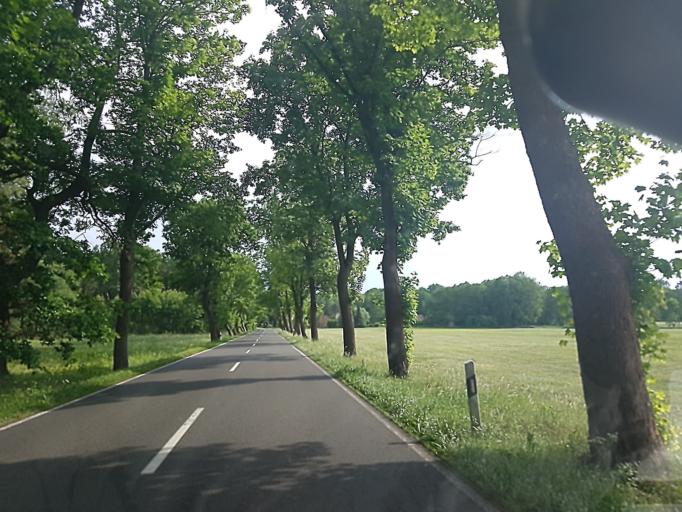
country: DE
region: Saxony-Anhalt
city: Nudersdorf
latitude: 51.9458
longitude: 12.6007
